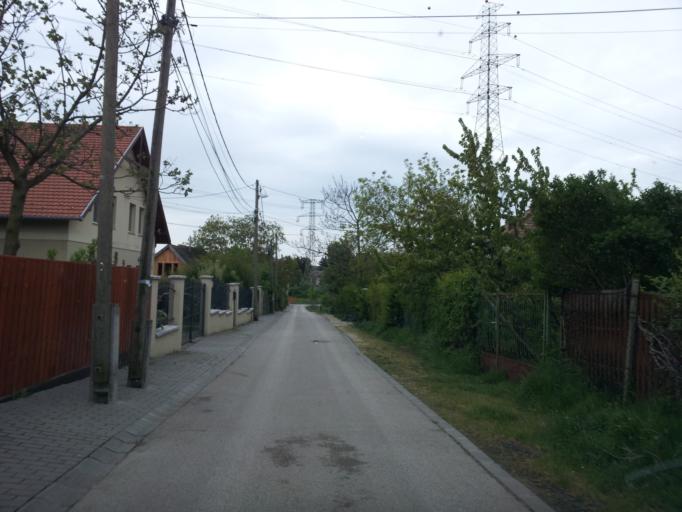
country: HU
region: Budapest
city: Budapest XXII. keruelet
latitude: 47.4332
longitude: 19.0147
